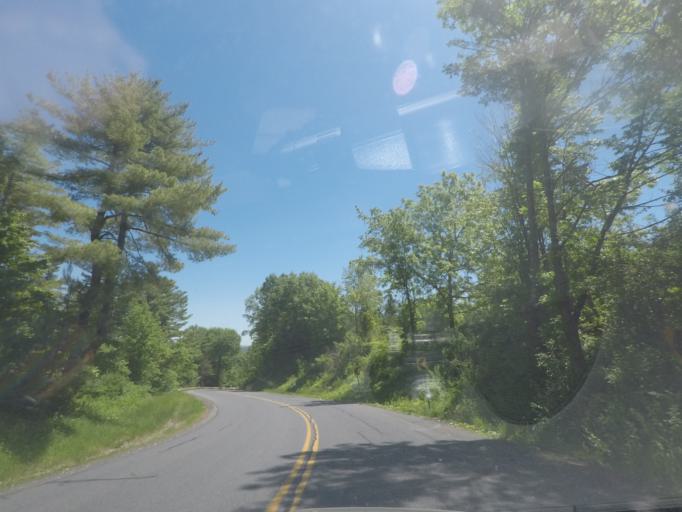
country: US
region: New York
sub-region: Saratoga County
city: Stillwater
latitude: 42.9345
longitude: -73.6789
